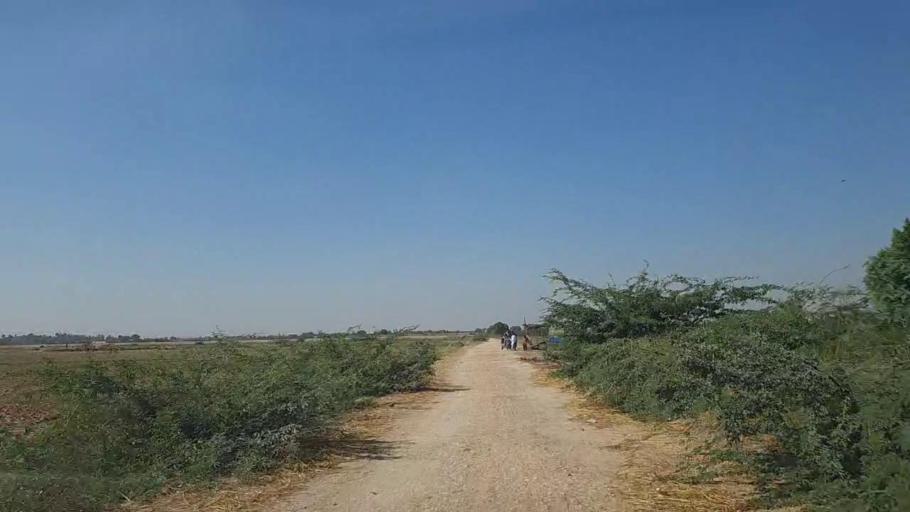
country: PK
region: Sindh
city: Thatta
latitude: 24.7687
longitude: 67.9482
